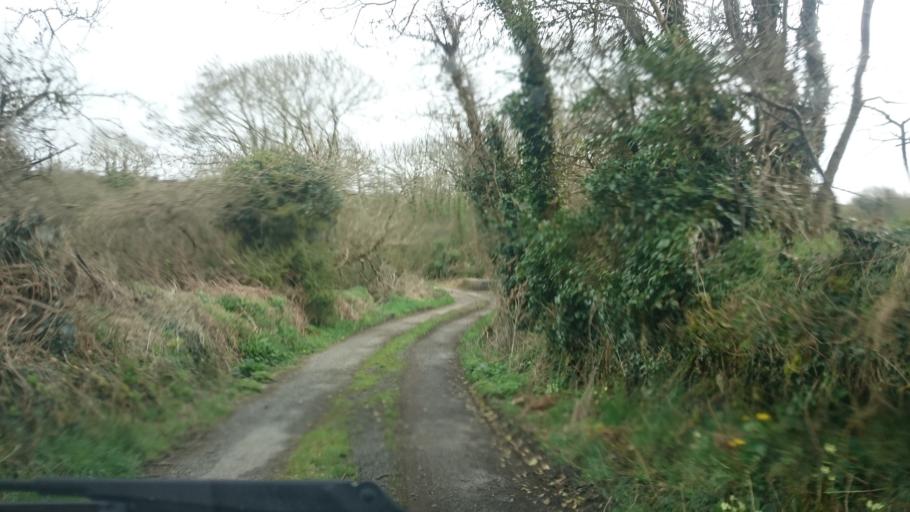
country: IE
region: Munster
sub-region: Waterford
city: Waterford
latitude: 52.2267
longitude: -7.0361
